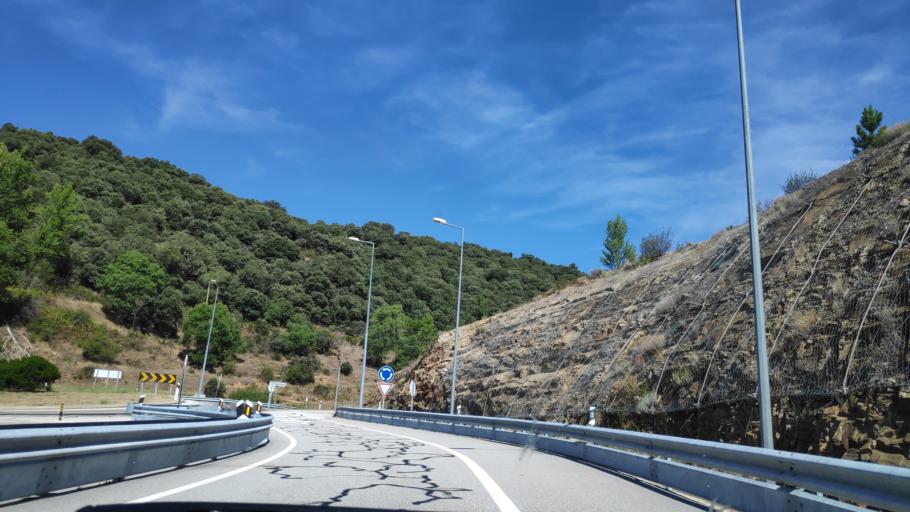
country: ES
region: Castille and Leon
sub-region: Provincia de Zamora
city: Trabazos
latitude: 41.7371
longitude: -6.5792
